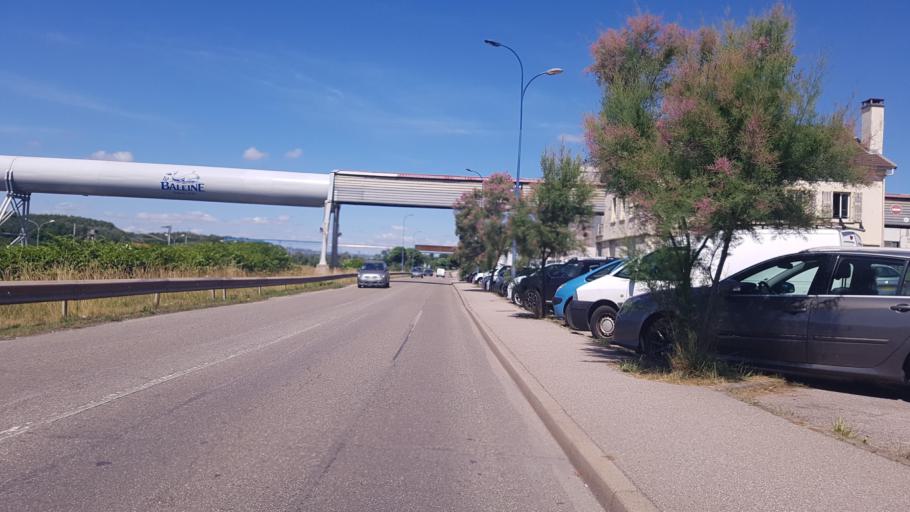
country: FR
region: Lorraine
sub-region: Departement de Meurthe-et-Moselle
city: Varangeville
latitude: 48.6367
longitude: 6.3100
